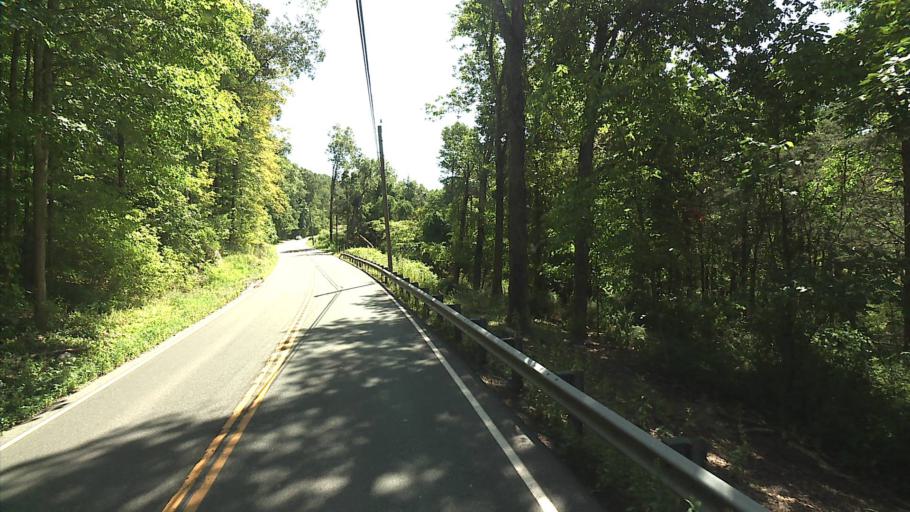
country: US
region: Connecticut
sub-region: New Haven County
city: Oxford
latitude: 41.4444
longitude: -73.1566
